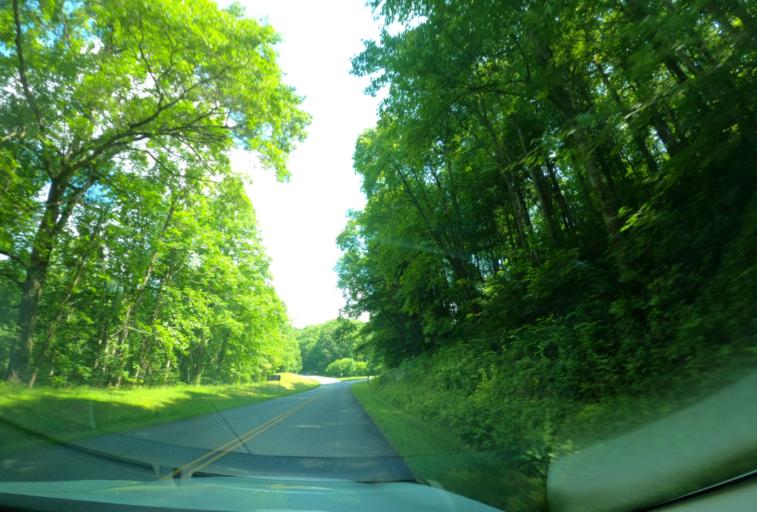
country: US
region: North Carolina
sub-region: Haywood County
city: Maggie Valley
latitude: 35.4395
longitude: -83.0800
